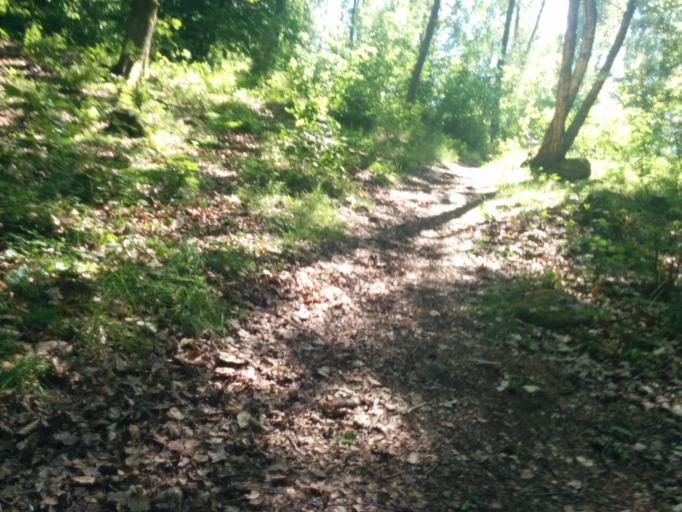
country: SE
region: Skane
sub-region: Lunds Kommun
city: Genarp
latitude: 55.5912
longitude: 13.3902
